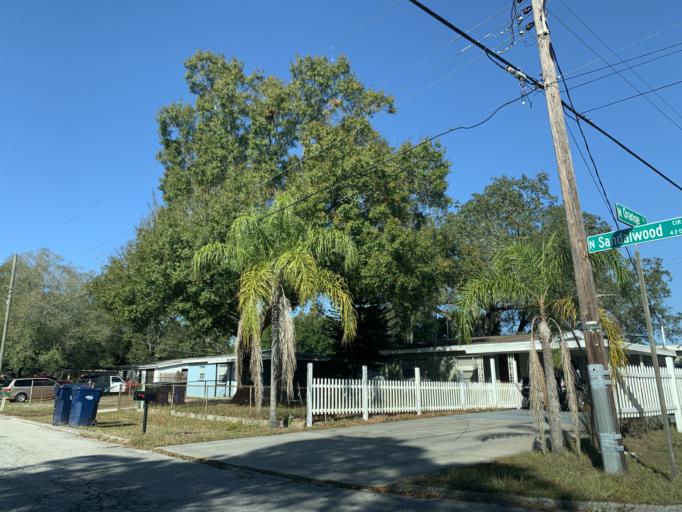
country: US
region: Florida
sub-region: Hillsborough County
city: Temple Terrace
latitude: 28.0282
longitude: -82.4110
